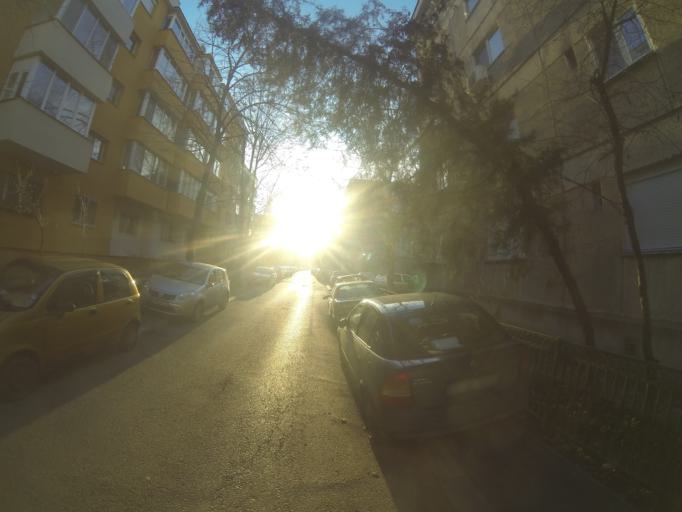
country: RO
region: Bucuresti
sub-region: Municipiul Bucuresti
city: Bucuresti
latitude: 44.4079
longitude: 26.0685
